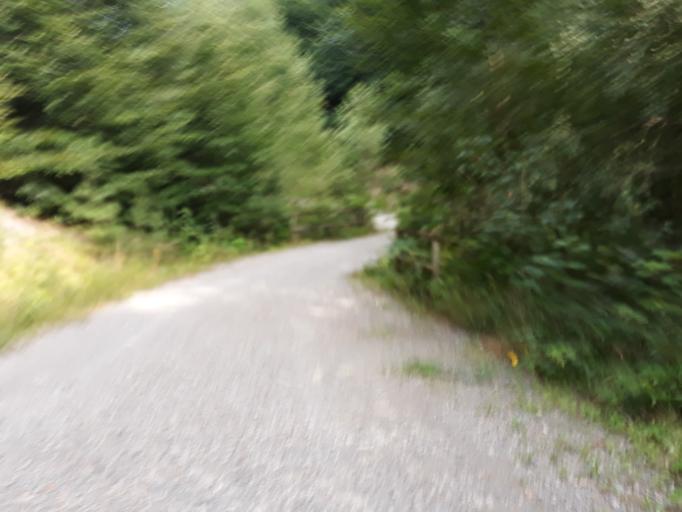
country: DE
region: Baden-Wuerttemberg
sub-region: Regierungsbezirk Stuttgart
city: Schonaich
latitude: 48.6822
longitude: 9.0452
